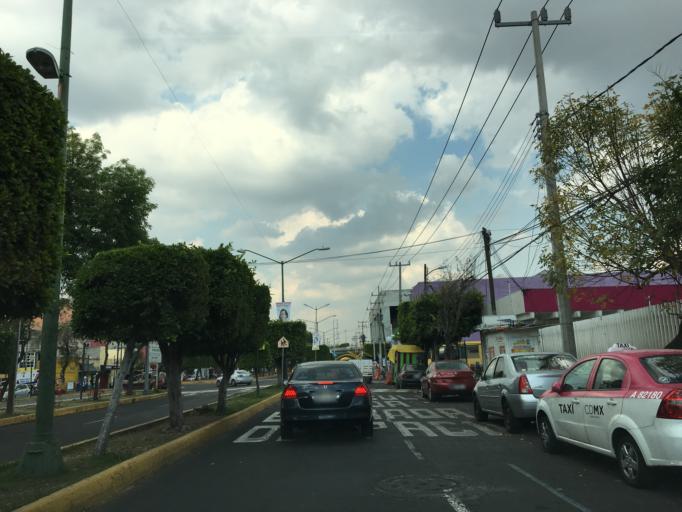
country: MX
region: Mexico City
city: Mexico City
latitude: 19.4182
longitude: -99.1151
